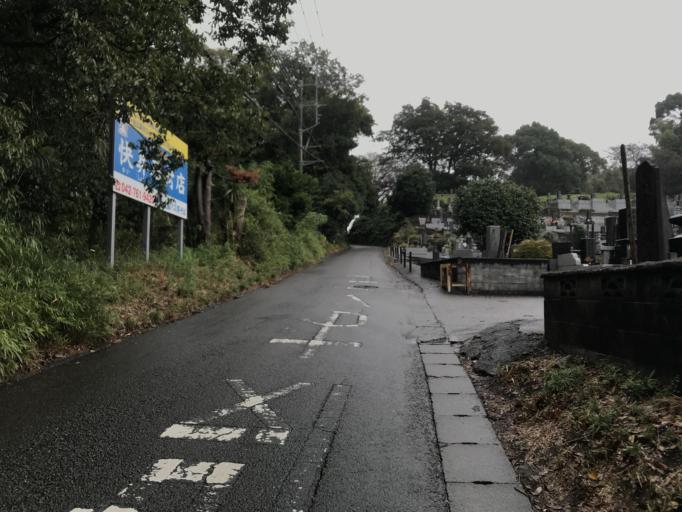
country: JP
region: Kanagawa
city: Zama
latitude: 35.5496
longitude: 139.3253
